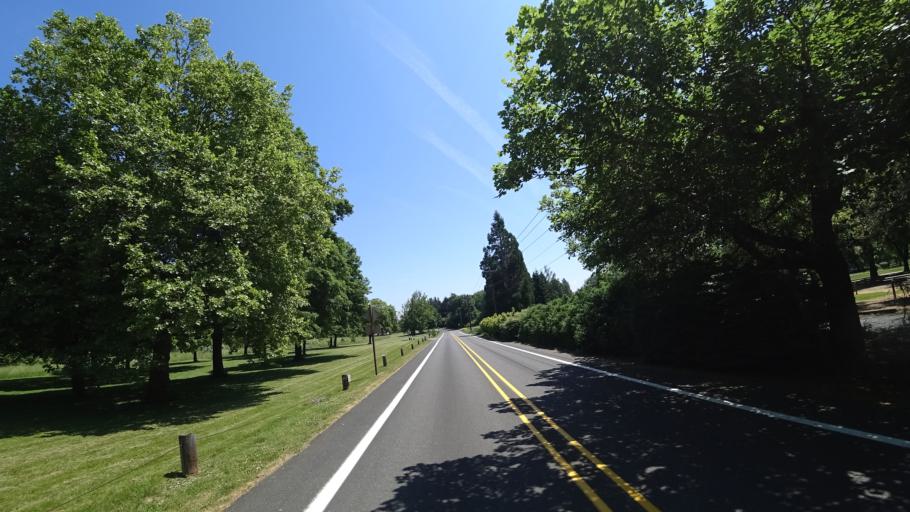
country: US
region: Oregon
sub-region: Multnomah County
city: Fairview
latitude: 45.5567
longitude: -122.4463
